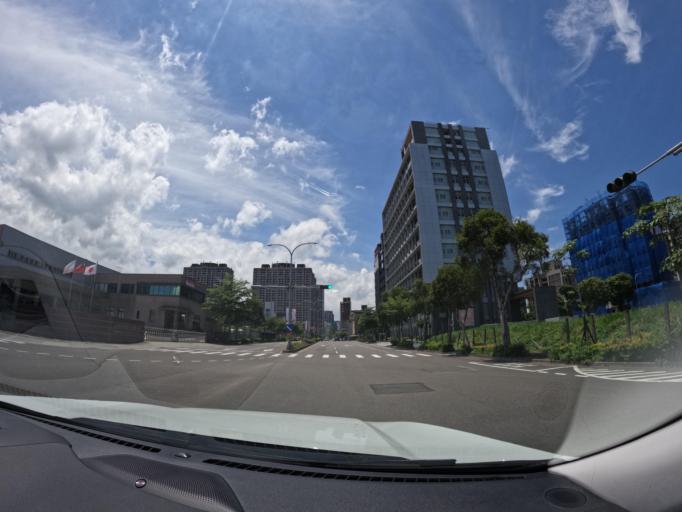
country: TW
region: Taipei
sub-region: Taipei
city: Banqiao
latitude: 25.0891
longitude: 121.3806
